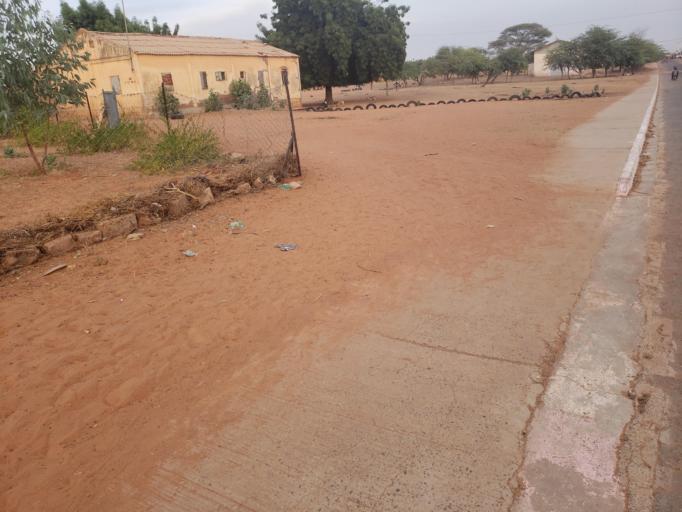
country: SN
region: Louga
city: Ndibene Dahra
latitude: 15.3990
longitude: -15.1114
